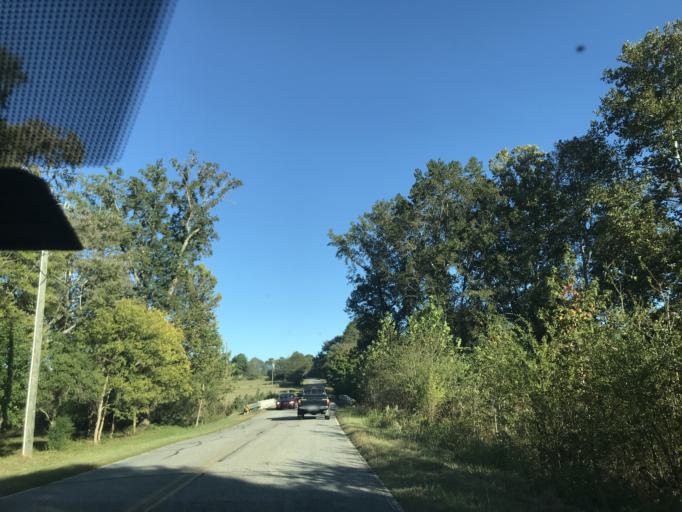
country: US
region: South Carolina
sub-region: Spartanburg County
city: Mayo
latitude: 35.1062
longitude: -81.8411
